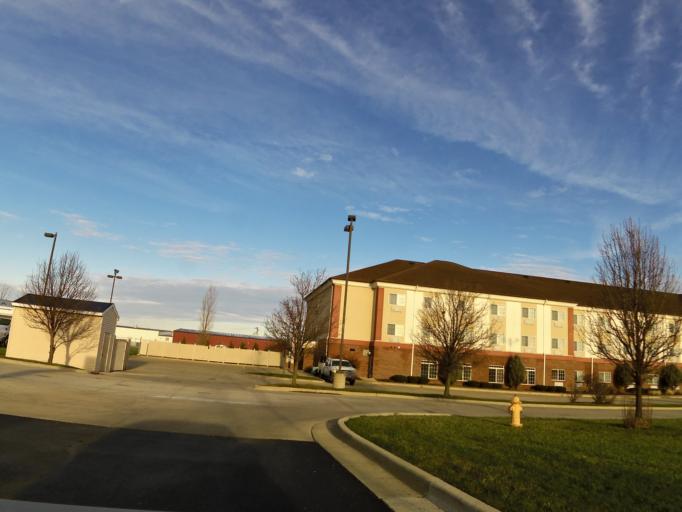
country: US
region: Illinois
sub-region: Vermilion County
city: Danville
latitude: 40.1219
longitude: -87.5436
